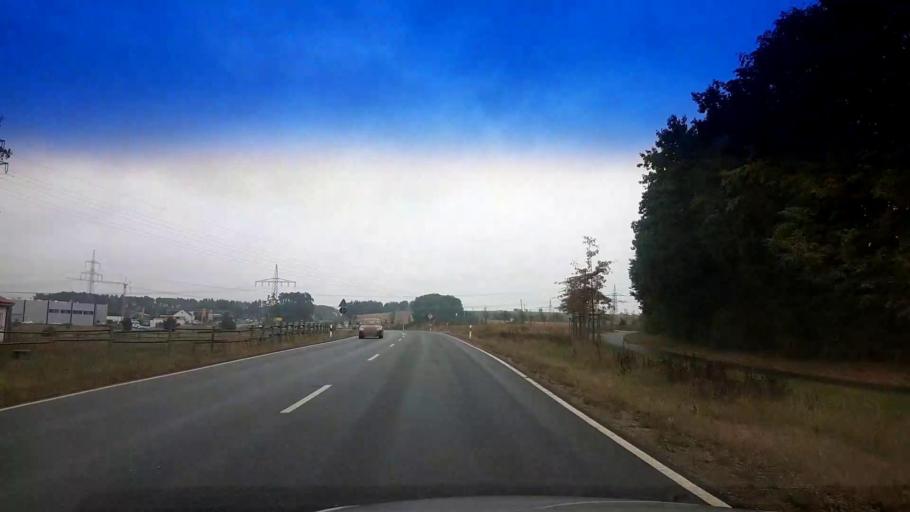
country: DE
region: Bavaria
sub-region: Upper Franconia
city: Forchheim
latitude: 49.7068
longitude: 11.0420
